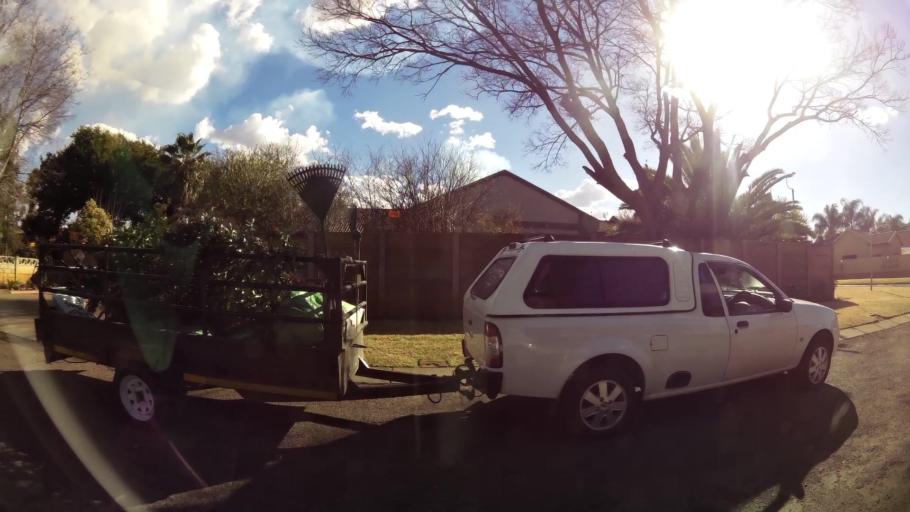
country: ZA
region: North-West
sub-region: Dr Kenneth Kaunda District Municipality
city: Klerksdorp
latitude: -26.8289
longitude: 26.6806
